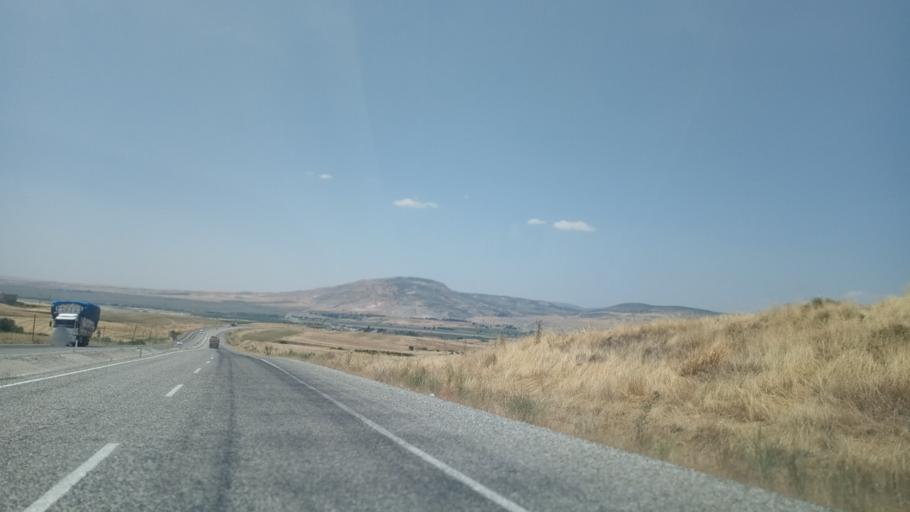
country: TR
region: Batman
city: Bekirhan
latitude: 38.1353
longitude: 41.2517
